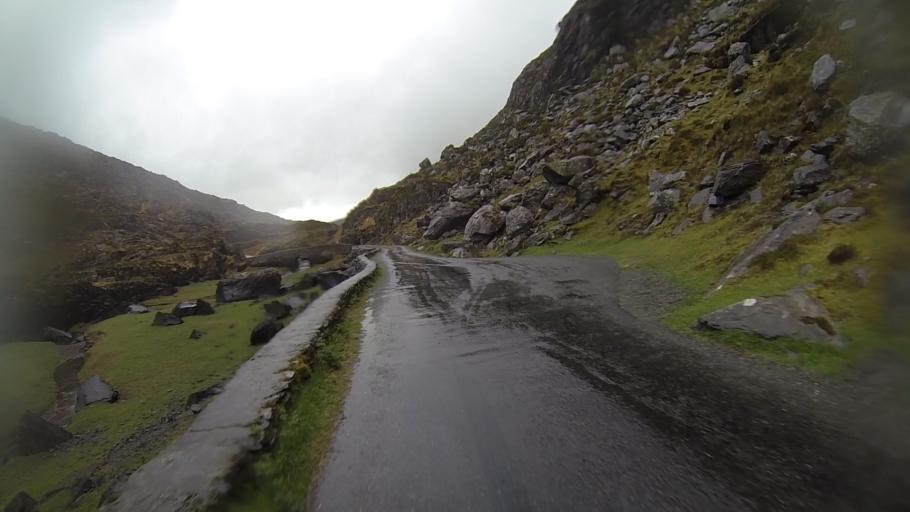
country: IE
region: Munster
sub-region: Ciarrai
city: Cill Airne
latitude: 52.0046
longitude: -9.6433
